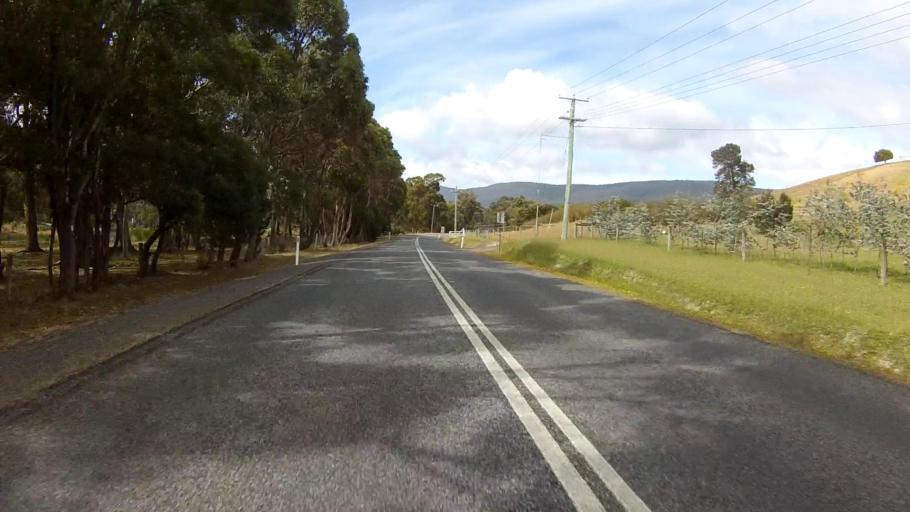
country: AU
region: Tasmania
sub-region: Kingborough
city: Kettering
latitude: -43.1500
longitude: 147.2400
